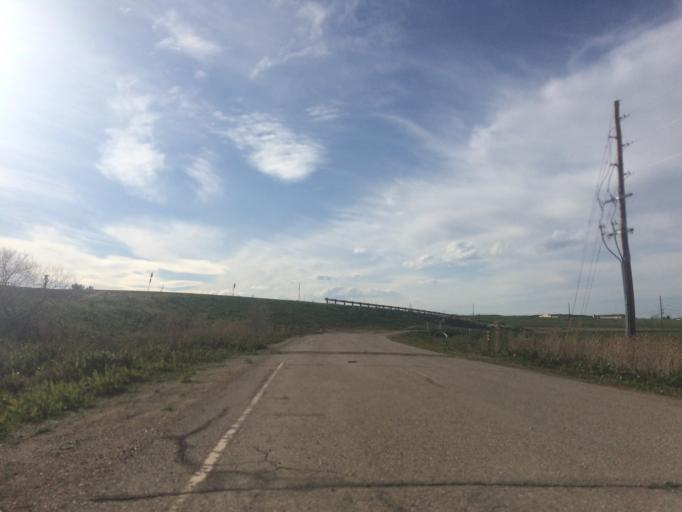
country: US
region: Colorado
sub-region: Broomfield County
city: Broomfield
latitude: 39.9323
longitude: -105.1179
